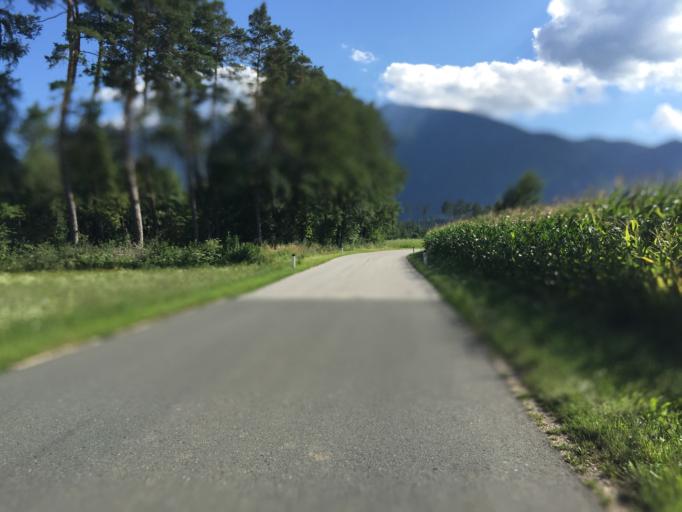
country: AT
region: Carinthia
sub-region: Politischer Bezirk Volkermarkt
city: Feistritz ob Bleiburg
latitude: 46.5676
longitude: 14.7701
